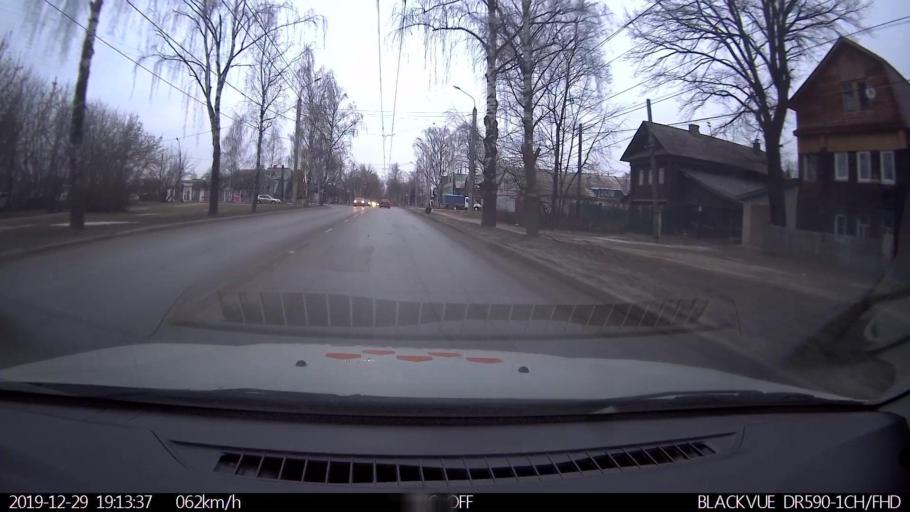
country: RU
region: Nizjnij Novgorod
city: Neklyudovo
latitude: 56.3634
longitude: 43.8549
